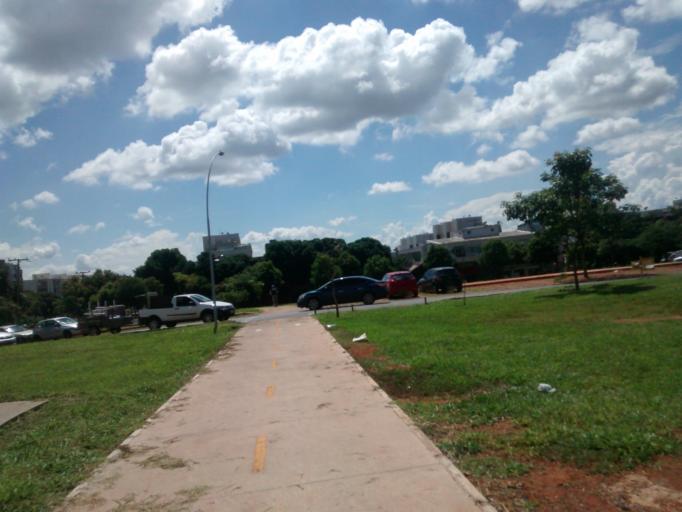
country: BR
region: Federal District
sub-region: Brasilia
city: Brasilia
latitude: -15.7604
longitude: -47.8879
